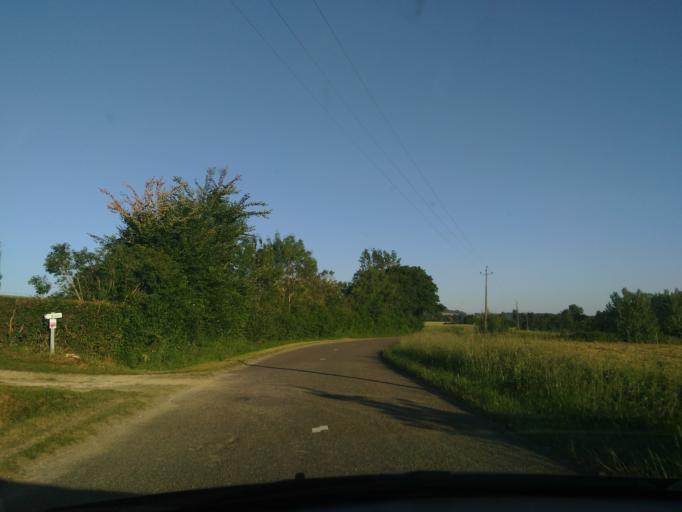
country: FR
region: Midi-Pyrenees
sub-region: Departement du Gers
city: Valence-sur-Baise
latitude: 43.8709
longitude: 0.4365
